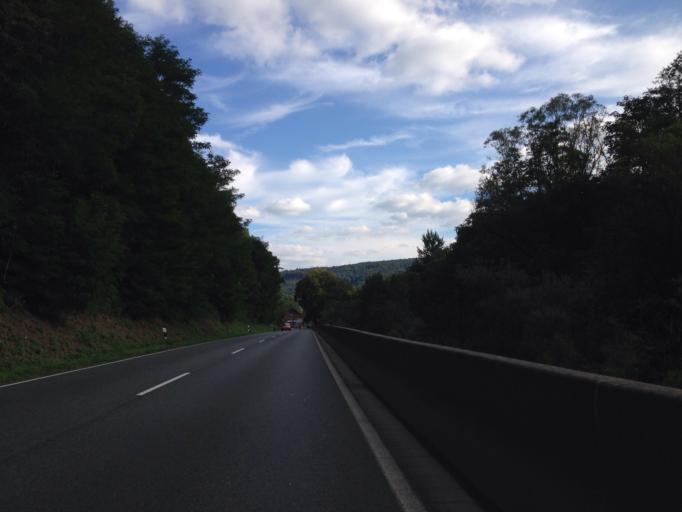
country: DE
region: Hesse
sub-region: Regierungsbezirk Giessen
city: Biedenkopf
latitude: 50.9245
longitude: 8.5016
